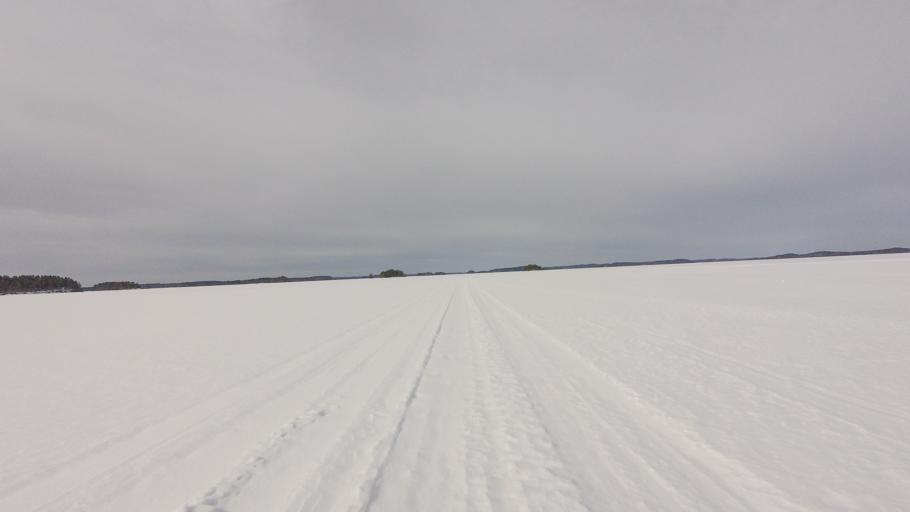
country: FI
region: Southern Savonia
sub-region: Savonlinna
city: Rantasalmi
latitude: 62.1026
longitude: 28.4380
